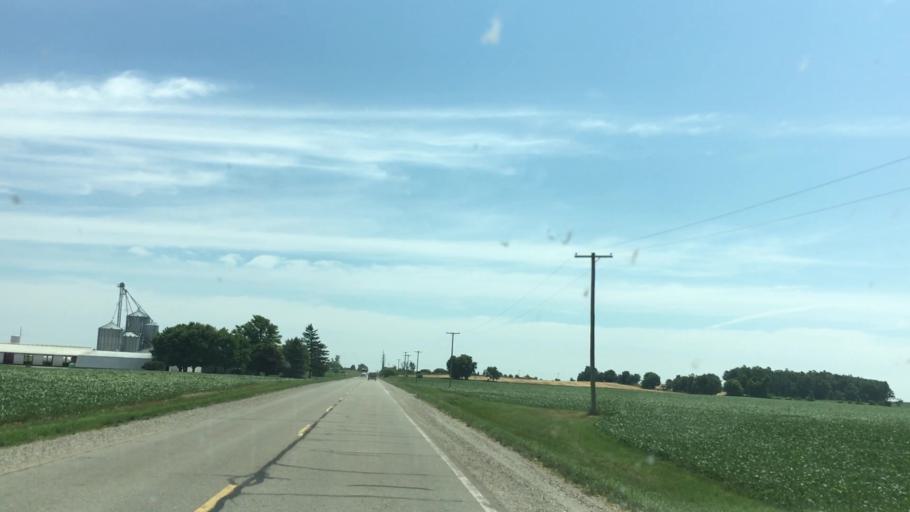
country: US
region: Michigan
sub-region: Sanilac County
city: Brown City
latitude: 43.2557
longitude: -83.0359
